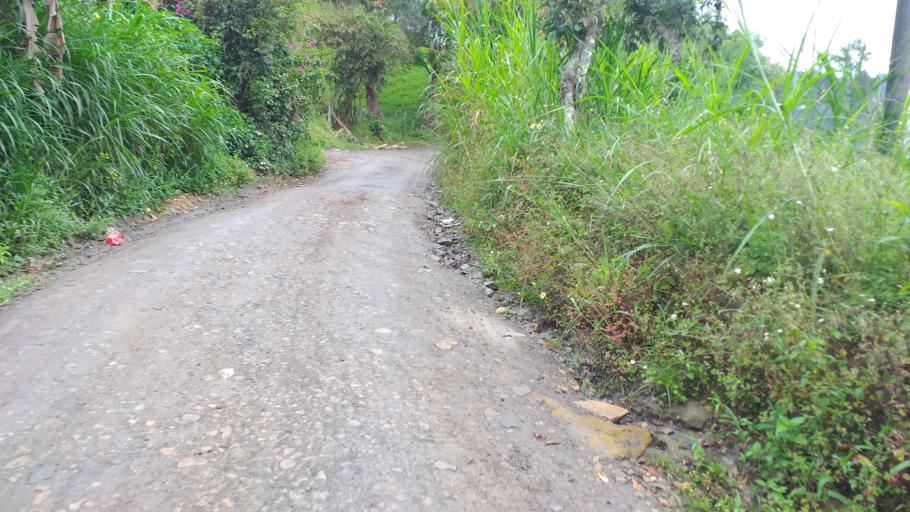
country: CO
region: Cundinamarca
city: Tenza
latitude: 5.1010
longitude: -73.4512
